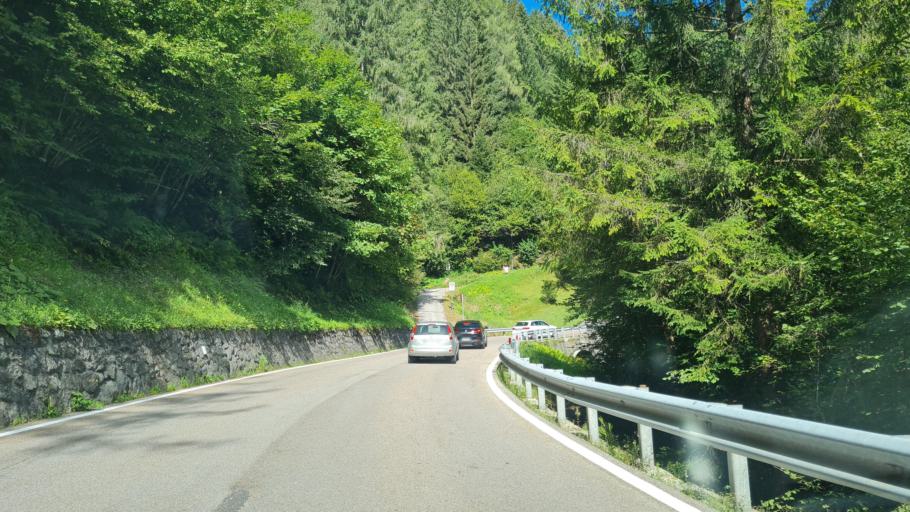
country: IT
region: Trentino-Alto Adige
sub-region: Provincia di Trento
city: Siror
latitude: 46.2042
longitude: 11.8191
